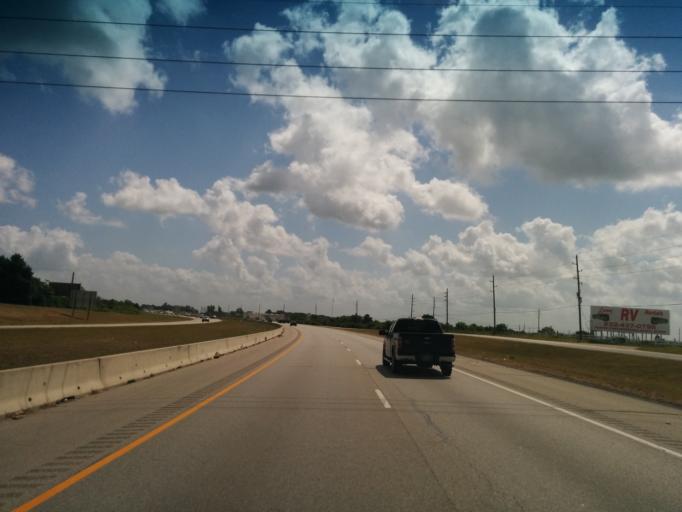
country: US
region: Texas
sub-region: Austin County
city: Sealy
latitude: 29.7675
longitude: -96.1426
